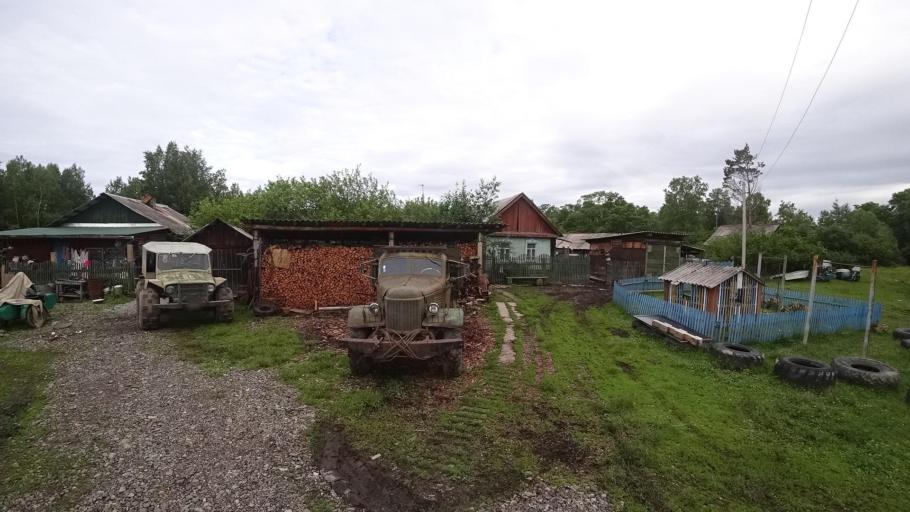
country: RU
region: Khabarovsk Krai
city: Amursk
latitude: 49.9068
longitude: 136.1326
